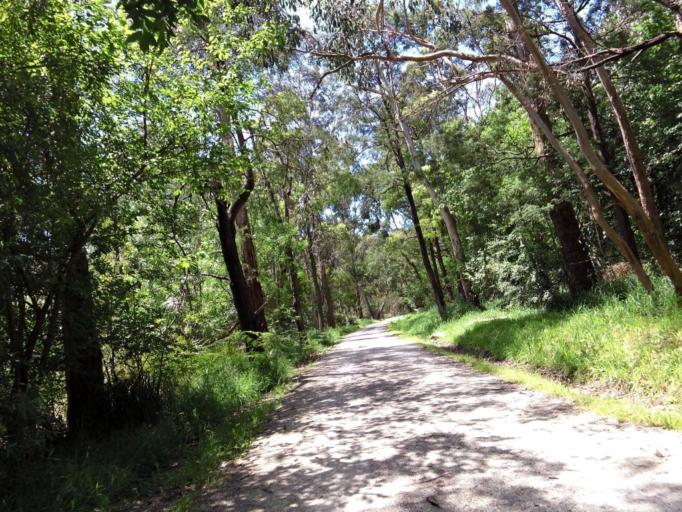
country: AU
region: Victoria
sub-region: Yarra Ranges
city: Mount Evelyn
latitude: -37.7713
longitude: 145.4477
